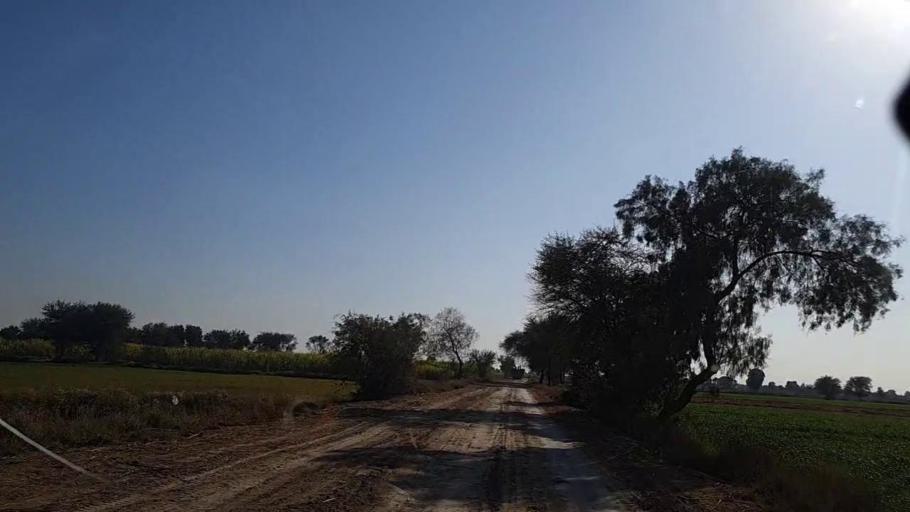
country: PK
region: Sindh
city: Khanpur
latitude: 27.7784
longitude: 69.3662
